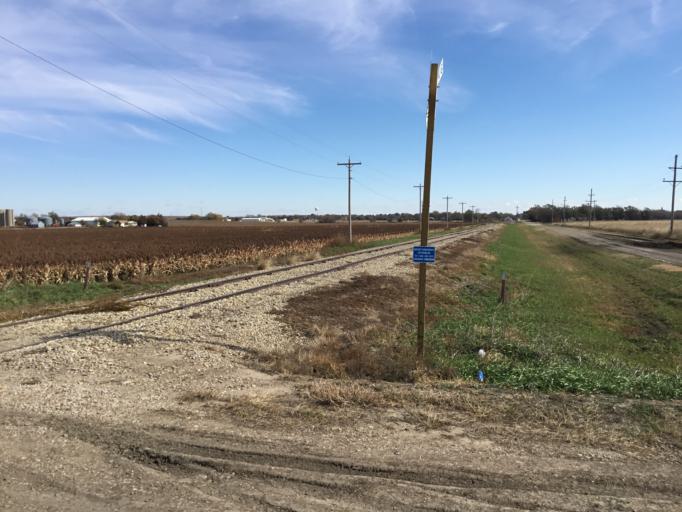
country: US
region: Kansas
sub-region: Lincoln County
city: Lincoln
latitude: 39.0450
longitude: -98.1701
